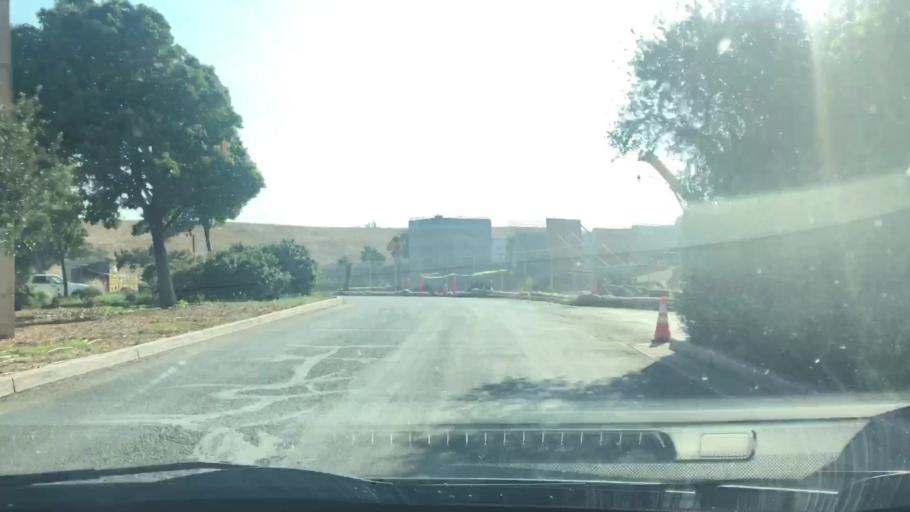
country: US
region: California
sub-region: Santa Clara County
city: Sunnyvale
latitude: 37.4187
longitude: -122.0124
